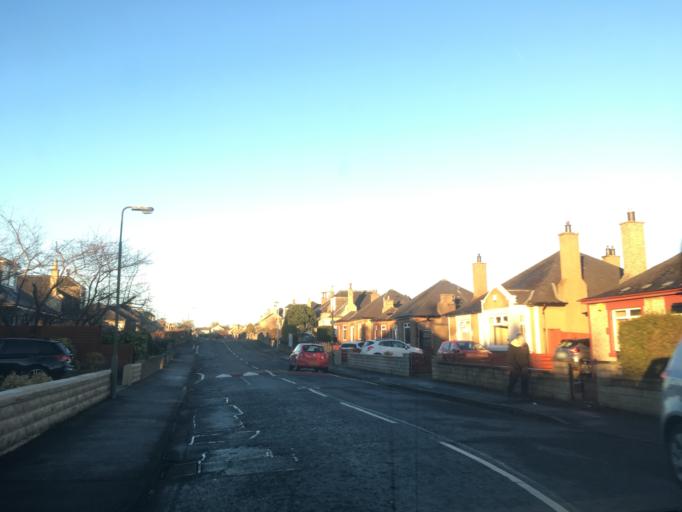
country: GB
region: Scotland
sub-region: Edinburgh
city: Currie
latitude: 55.9421
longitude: -3.3016
